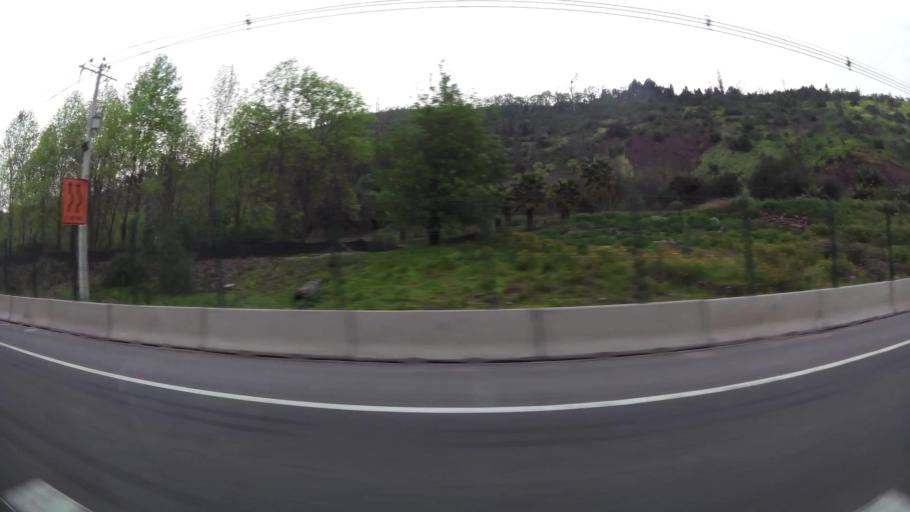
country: CL
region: Santiago Metropolitan
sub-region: Provincia de Santiago
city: Villa Presidente Frei, Nunoa, Santiago, Chile
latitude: -33.4062
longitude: -70.6050
